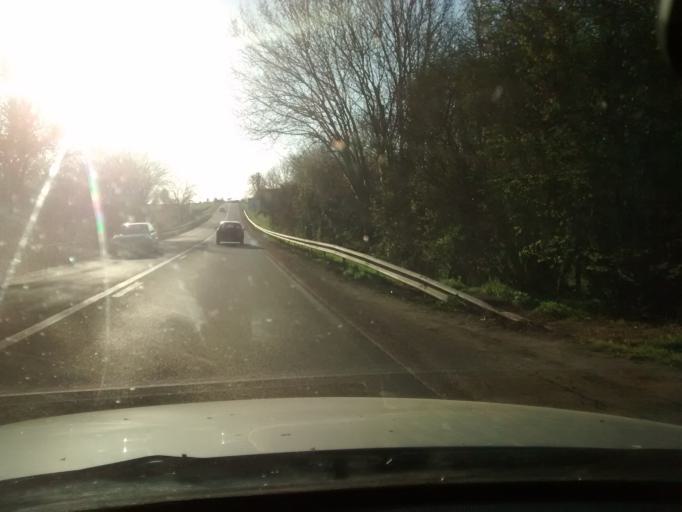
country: FR
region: Pays de la Loire
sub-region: Departement de la Sarthe
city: Trange
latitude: 48.0203
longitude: 0.1150
